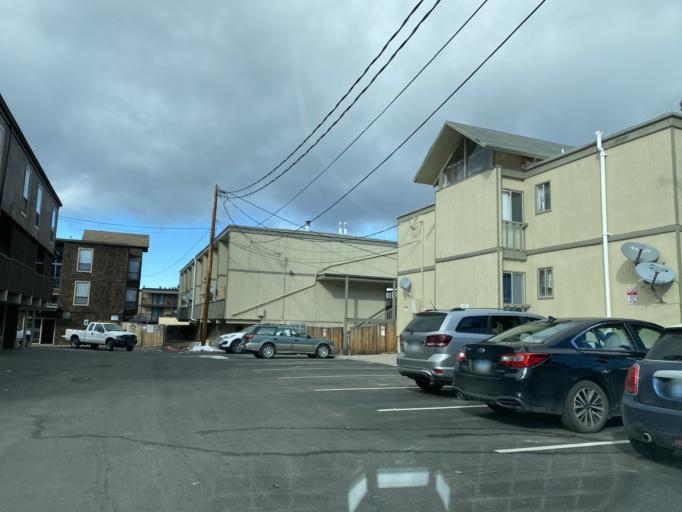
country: US
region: Nevada
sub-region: Douglas County
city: Kingsbury
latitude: 38.9714
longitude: -119.9394
